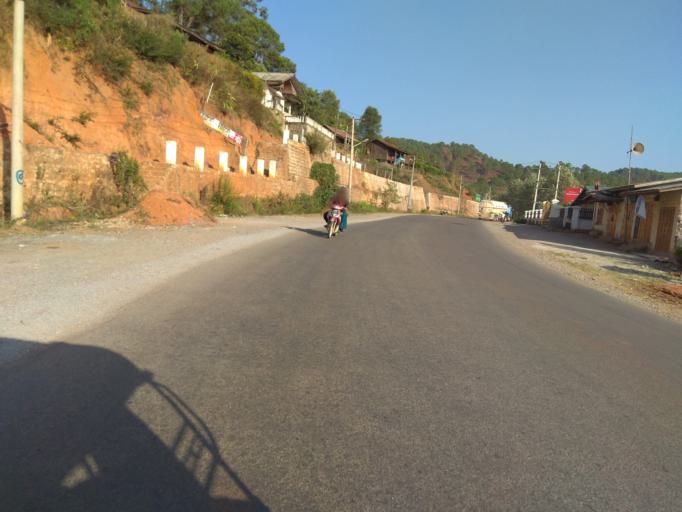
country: MM
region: Mandalay
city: Yamethin
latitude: 20.6352
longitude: 96.5751
